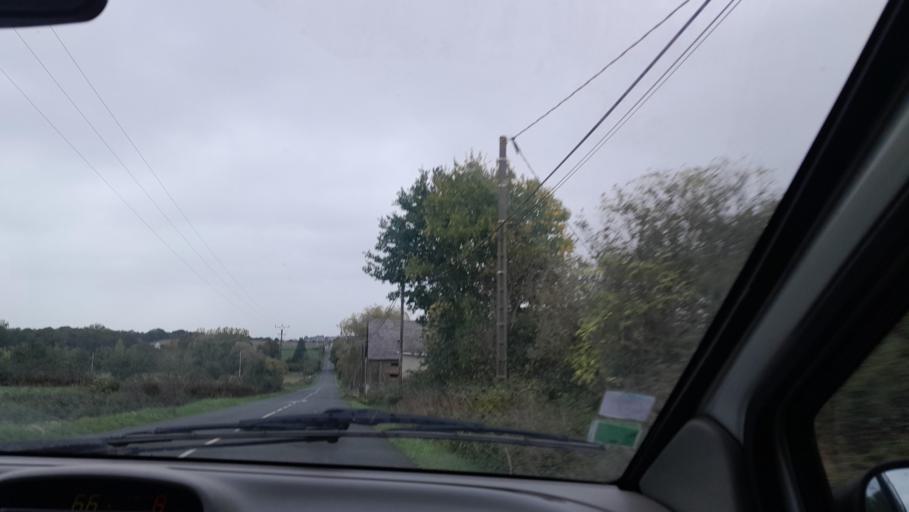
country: FR
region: Pays de la Loire
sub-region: Departement de Maine-et-Loire
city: Pouance
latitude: 47.7189
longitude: -1.1778
